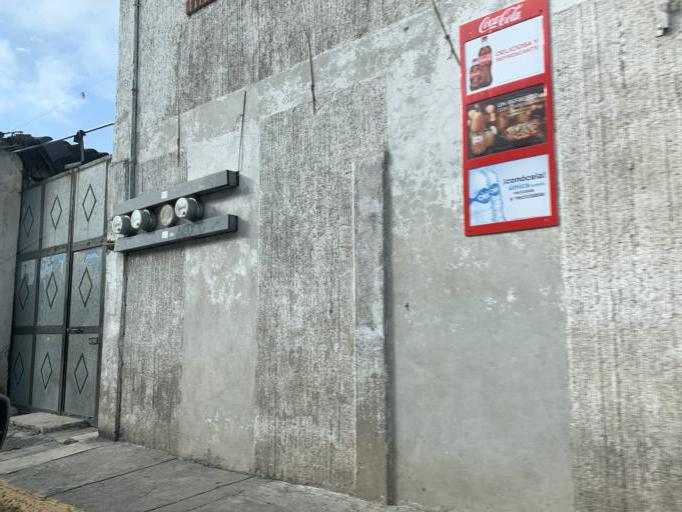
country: MX
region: Puebla
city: San Andres Cholula
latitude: 19.0504
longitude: -98.2935
